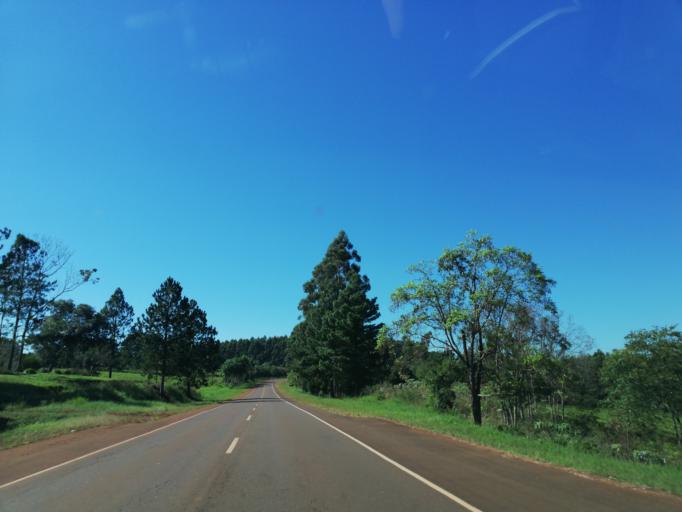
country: AR
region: Misiones
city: Dos de Mayo
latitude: -27.0695
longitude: -54.4121
